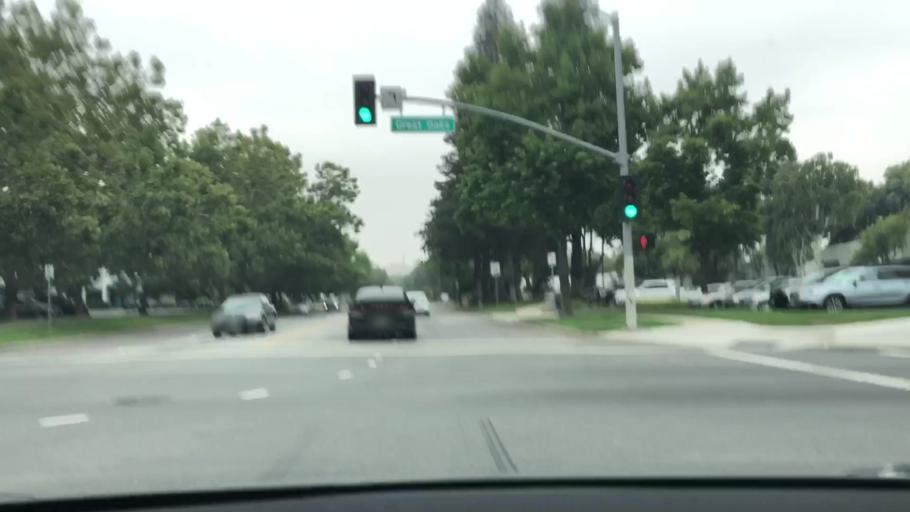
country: US
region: California
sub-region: Santa Clara County
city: Seven Trees
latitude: 37.2330
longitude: -121.7799
